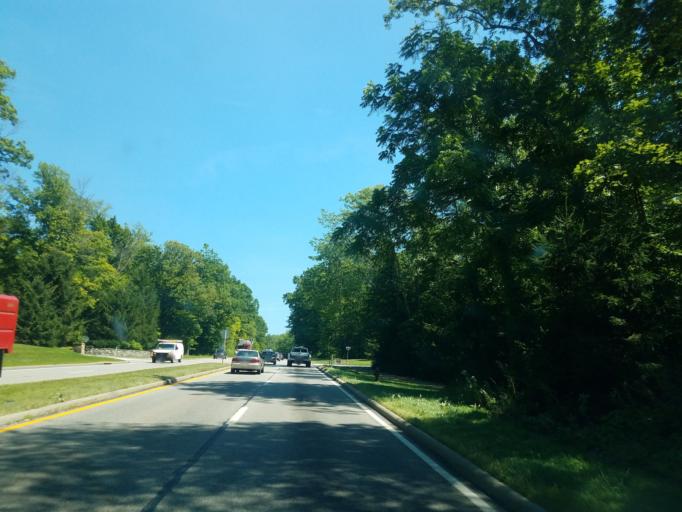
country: US
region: Ohio
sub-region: Cuyahoga County
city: Gates Mills
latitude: 41.5260
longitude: -81.4003
